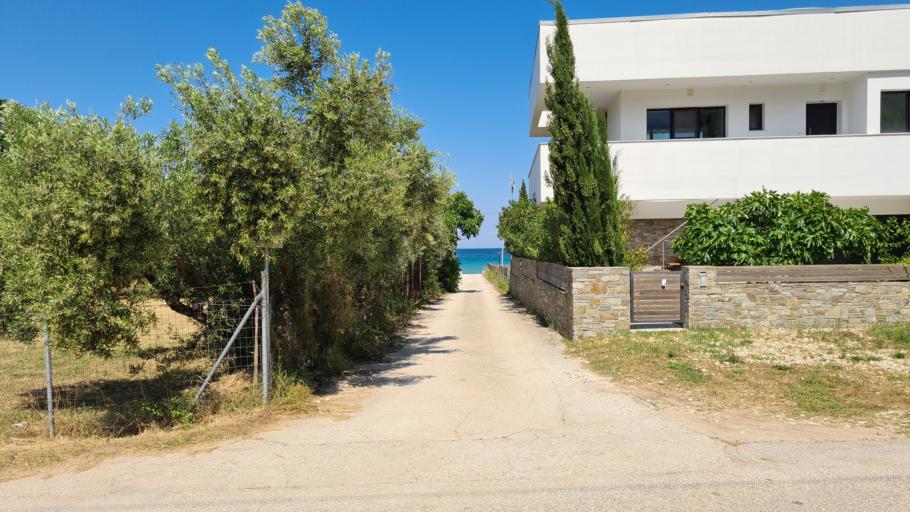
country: GR
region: East Macedonia and Thrace
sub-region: Nomos Kavalas
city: Potamia
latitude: 40.7114
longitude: 24.7577
